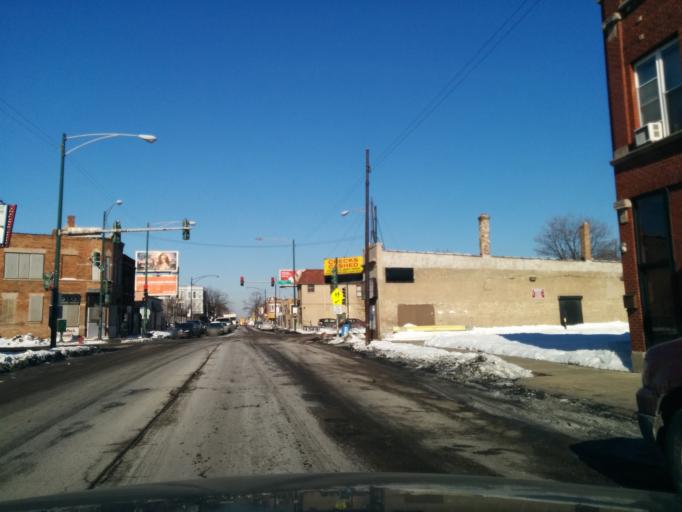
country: US
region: Illinois
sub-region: Cook County
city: Oak Park
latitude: 41.9040
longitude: -87.7209
